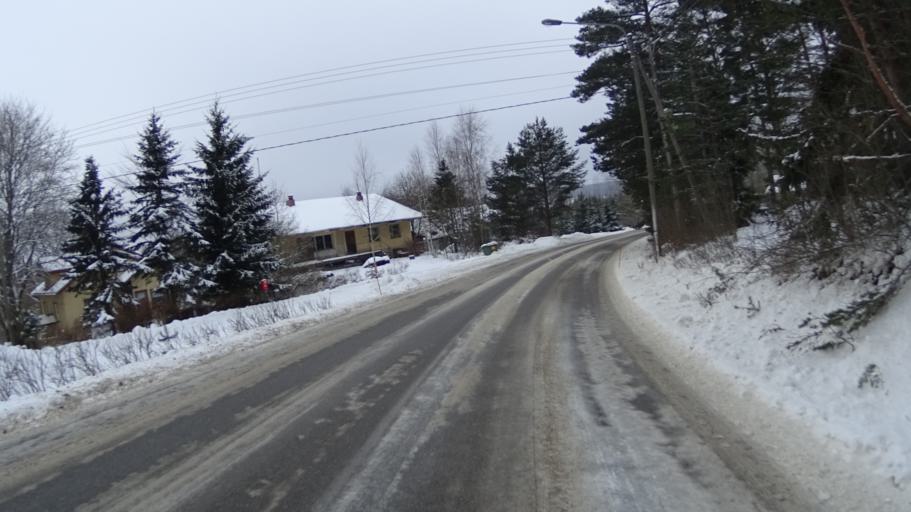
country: FI
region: Uusimaa
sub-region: Helsinki
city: Karkkila
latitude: 60.4863
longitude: 24.1216
